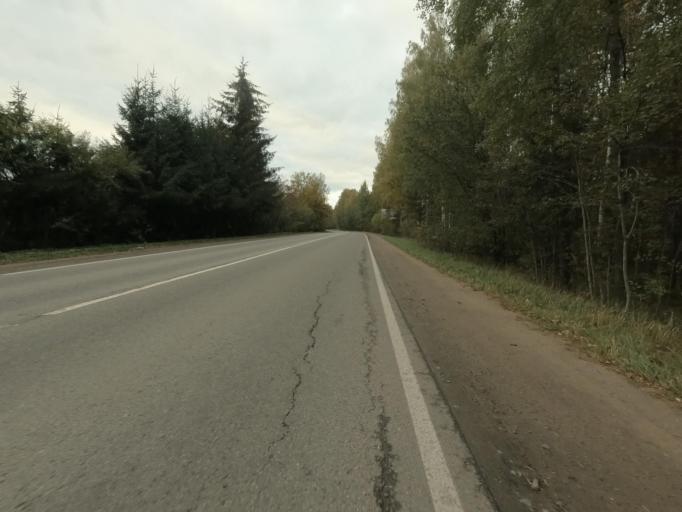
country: RU
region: Leningrad
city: Pavlovo
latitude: 59.7899
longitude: 30.9615
